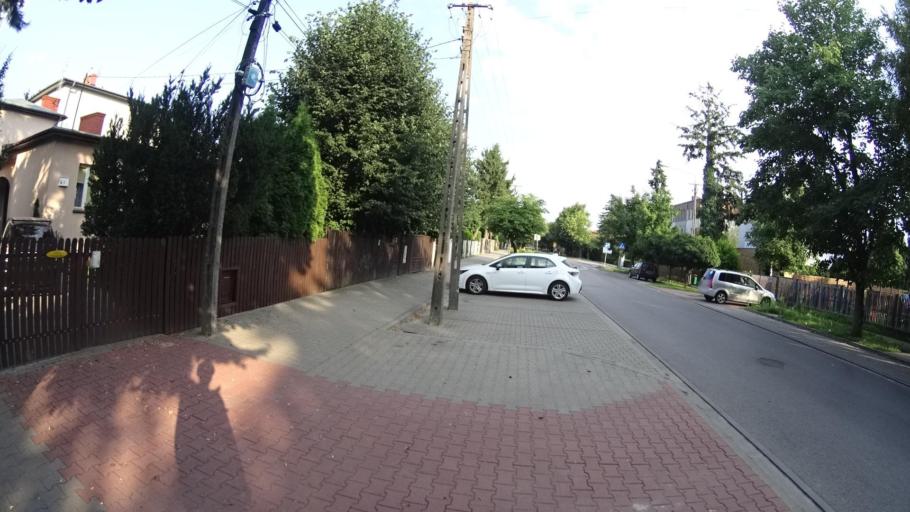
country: PL
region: Masovian Voivodeship
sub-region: Powiat pruszkowski
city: Michalowice
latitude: 52.1712
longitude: 20.8856
